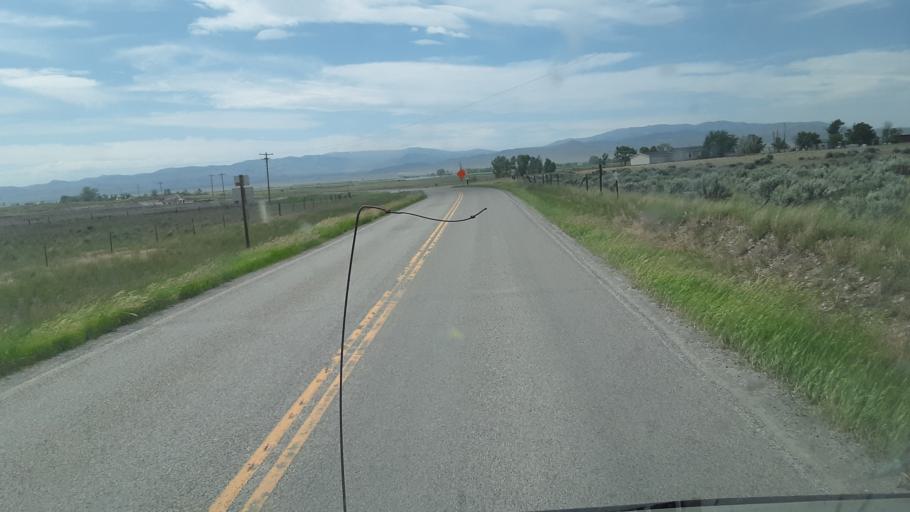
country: US
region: Montana
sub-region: Broadwater County
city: Townsend
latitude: 46.1729
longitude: -111.4493
